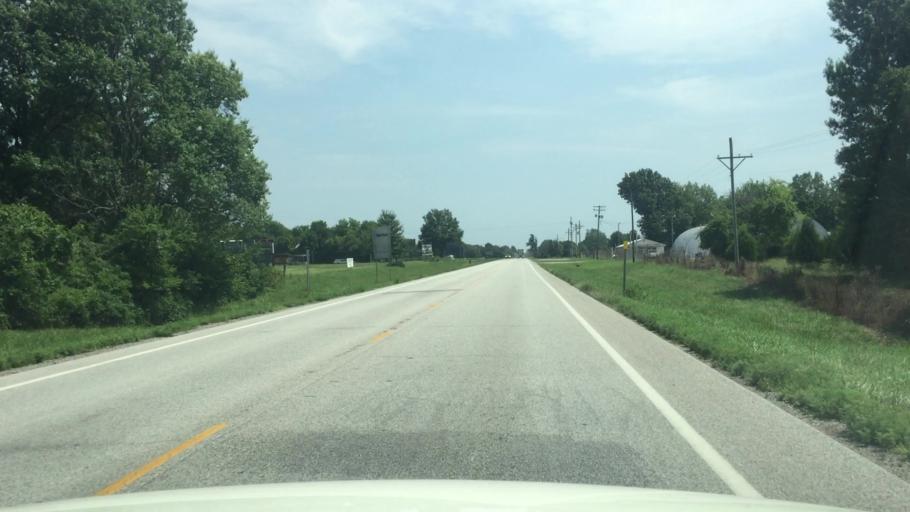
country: US
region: Kansas
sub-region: Cherokee County
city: Columbus
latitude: 37.1781
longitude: -94.8168
